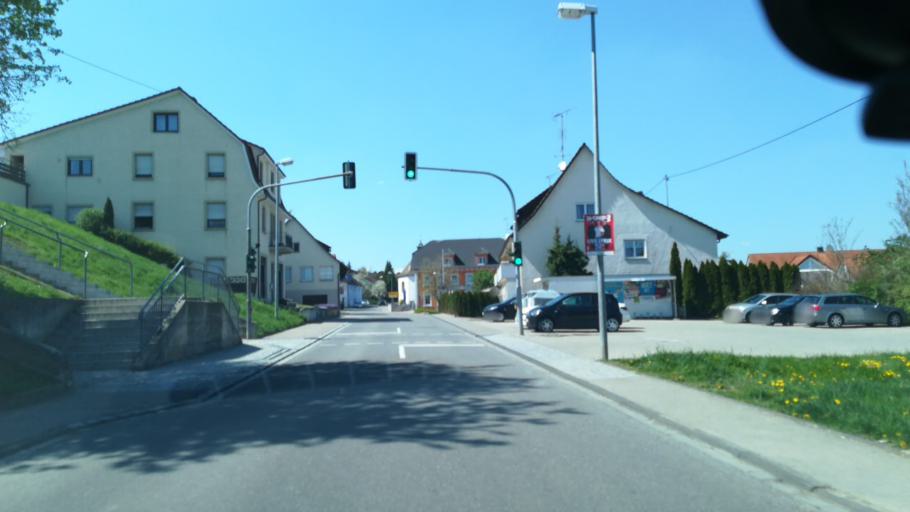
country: DE
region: Baden-Wuerttemberg
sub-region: Freiburg Region
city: Muhlhausen-Ehingen
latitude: 47.8112
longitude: 8.8060
